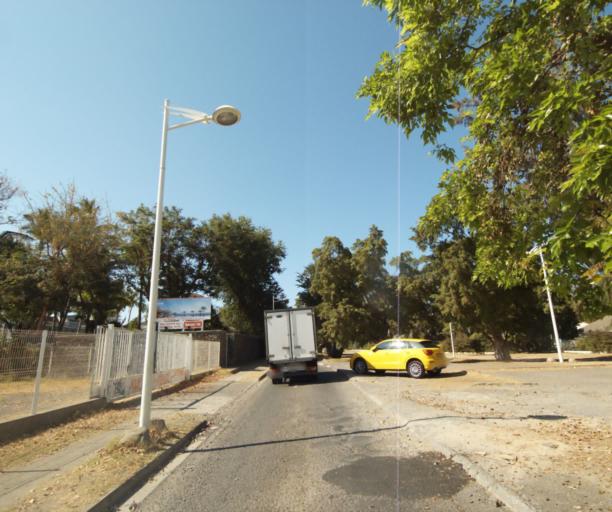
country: RE
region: Reunion
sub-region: Reunion
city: Saint-Paul
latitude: -21.0705
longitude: 55.2228
